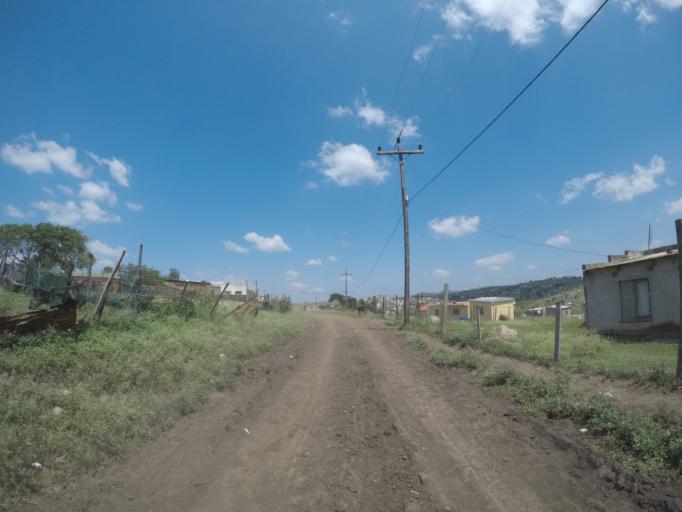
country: ZA
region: KwaZulu-Natal
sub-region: uThungulu District Municipality
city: Empangeni
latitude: -28.6029
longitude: 31.7418
